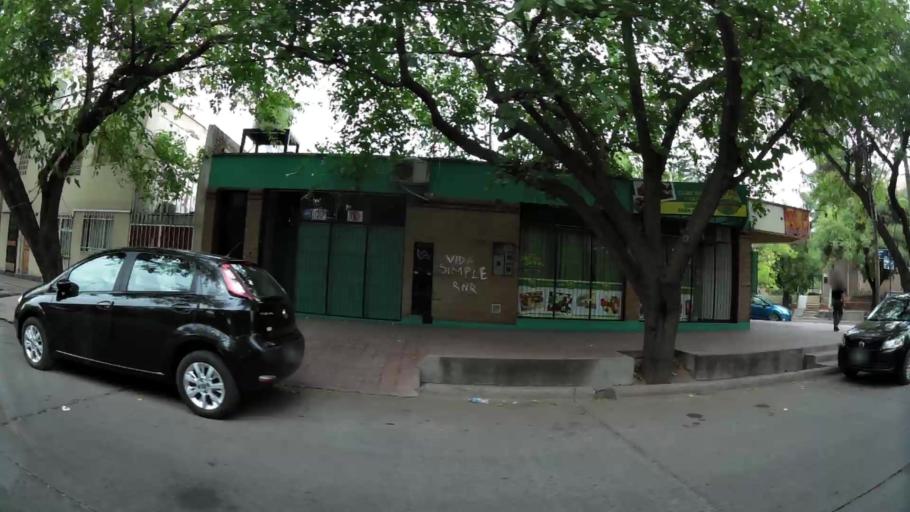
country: AR
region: Mendoza
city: Mendoza
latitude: -32.8753
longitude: -68.8378
